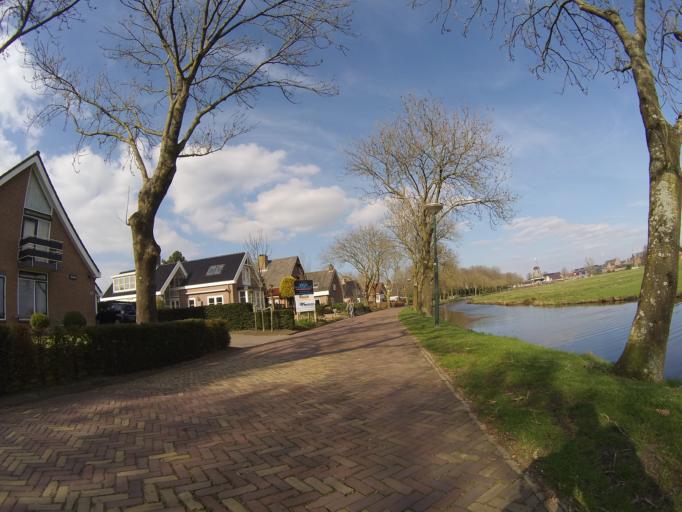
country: NL
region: Utrecht
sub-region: Gemeente Bunschoten
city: Bunschoten
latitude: 52.2405
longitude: 5.3694
